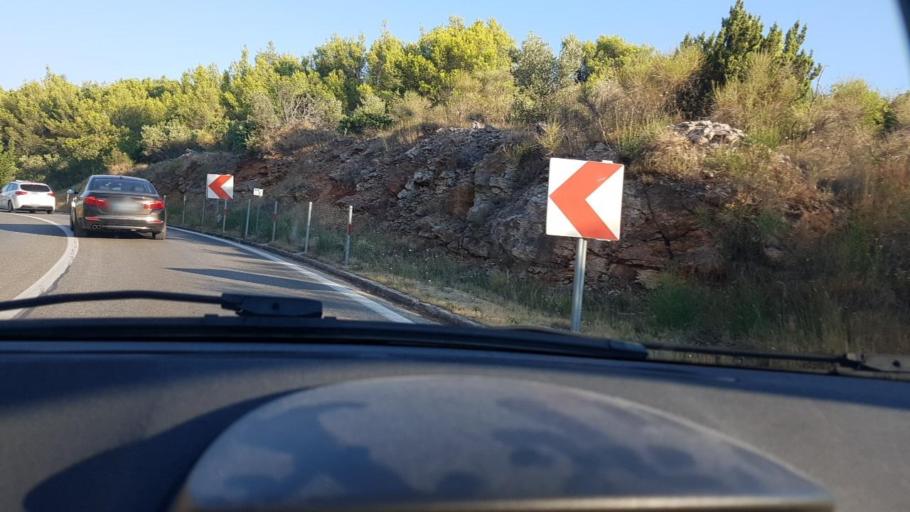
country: HR
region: Sibensko-Kniniska
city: Murter
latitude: 43.7969
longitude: 15.6172
